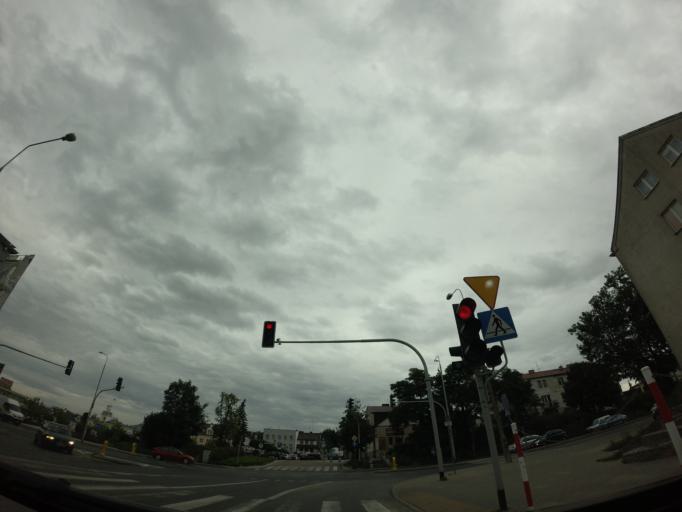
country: PL
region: Masovian Voivodeship
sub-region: Powiat ciechanowski
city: Ciechanow
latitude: 52.8813
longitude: 20.6198
